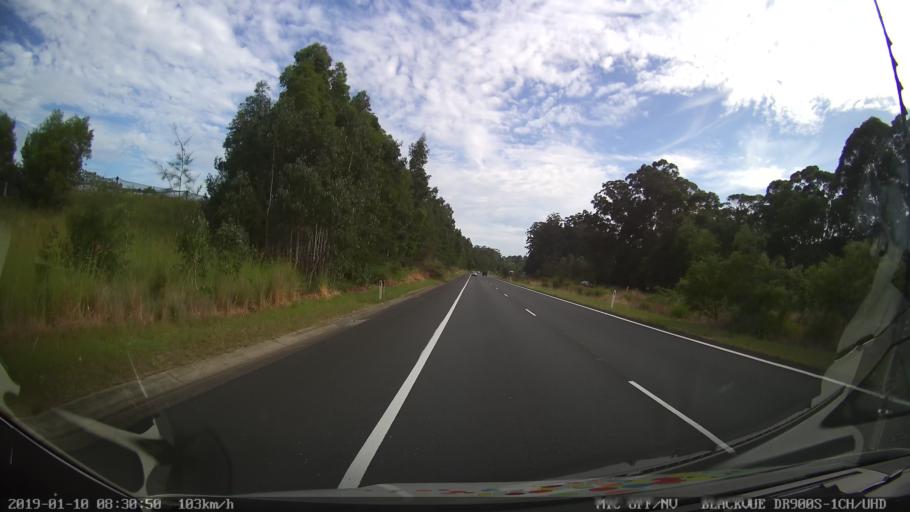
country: AU
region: New South Wales
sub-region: Coffs Harbour
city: Bonville
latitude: -30.3650
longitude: 153.0549
